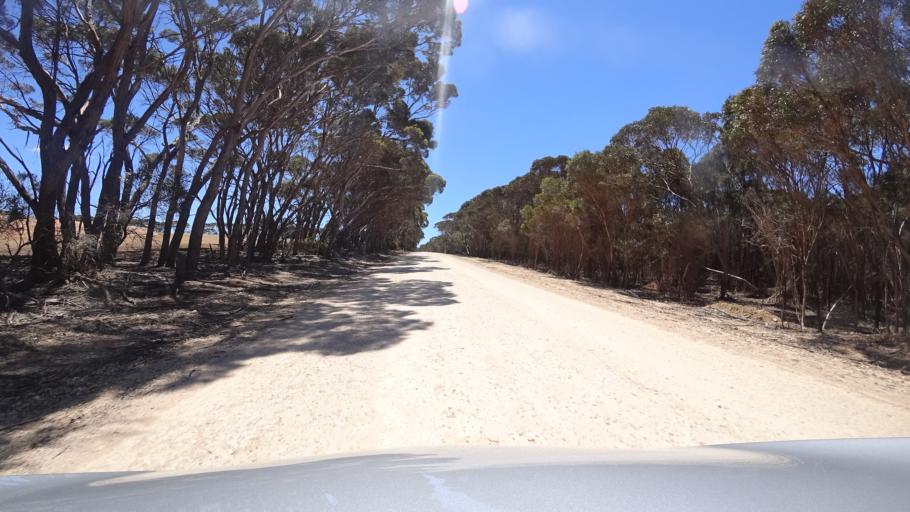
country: AU
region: South Australia
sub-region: Yankalilla
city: Normanville
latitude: -35.7823
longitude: 138.0580
